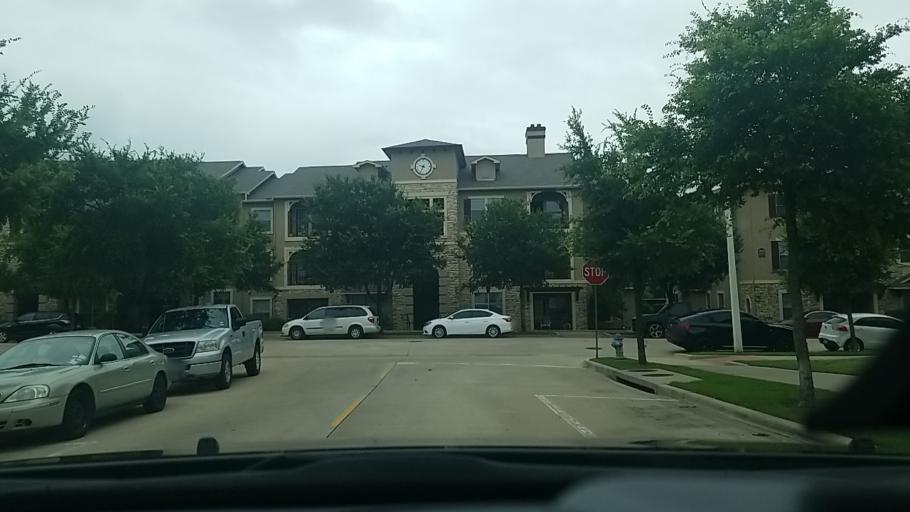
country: US
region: Texas
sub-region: Denton County
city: Corinth
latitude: 33.1861
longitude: -97.0924
